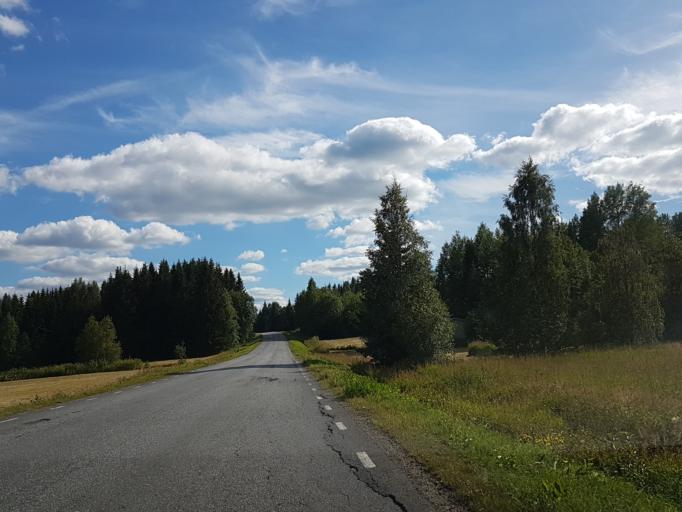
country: SE
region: Vaesterbotten
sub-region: Skelleftea Kommun
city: Burtraesk
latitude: 64.3173
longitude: 20.5316
